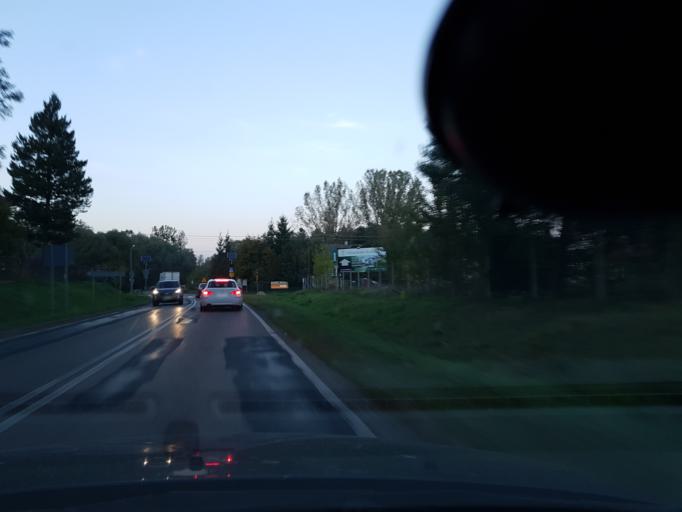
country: PL
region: Masovian Voivodeship
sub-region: Powiat zyrardowski
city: Radziejowice
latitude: 52.0432
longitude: 20.5905
